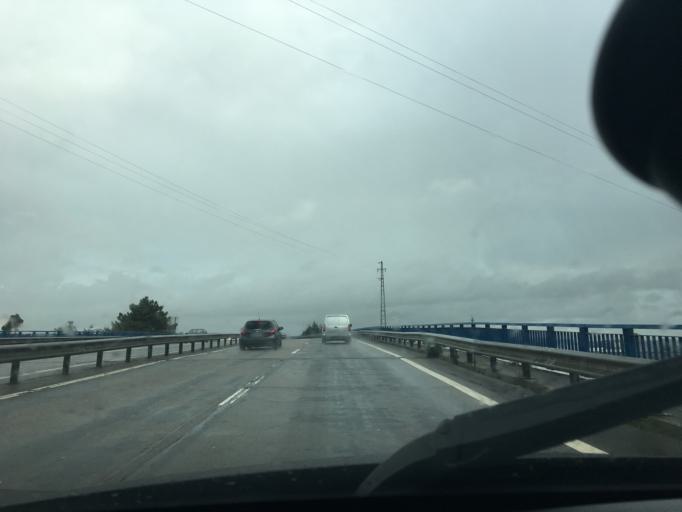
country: PT
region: Porto
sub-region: Matosinhos
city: Santa Cruz do Bispo
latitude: 41.2317
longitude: -8.6672
